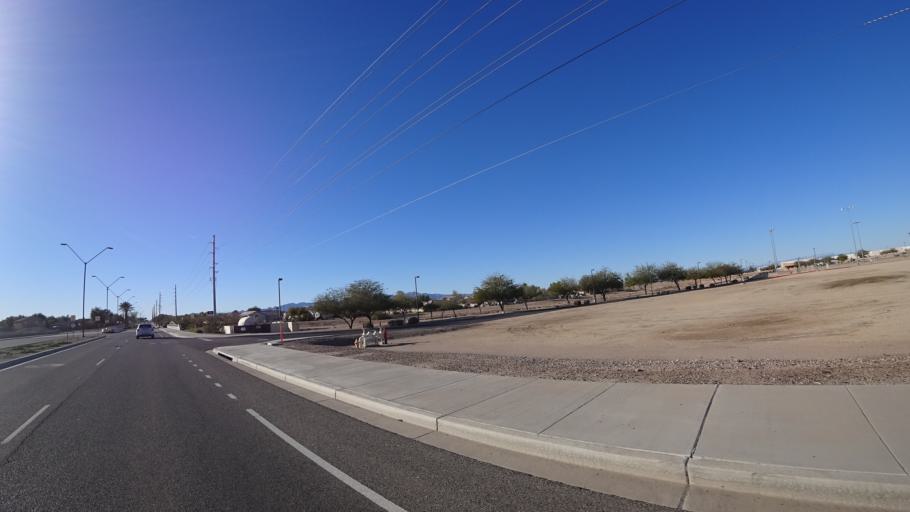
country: US
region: Arizona
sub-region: Maricopa County
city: Goodyear
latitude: 33.4500
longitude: -112.3811
